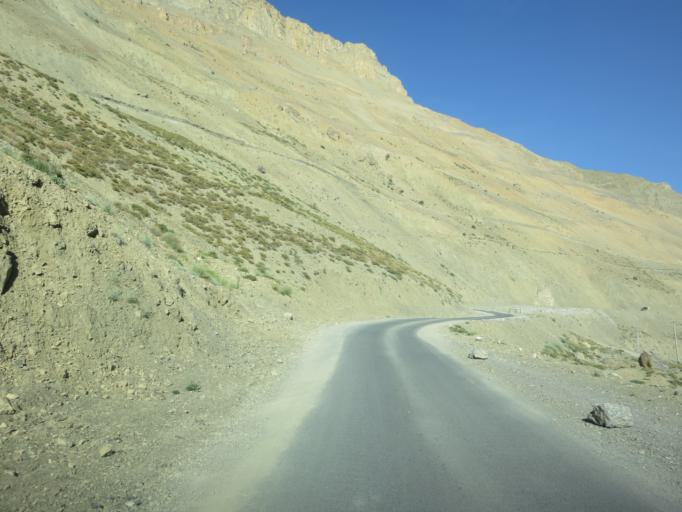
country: IN
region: Himachal Pradesh
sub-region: Shimla
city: Sarahan
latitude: 32.2437
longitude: 78.0554
